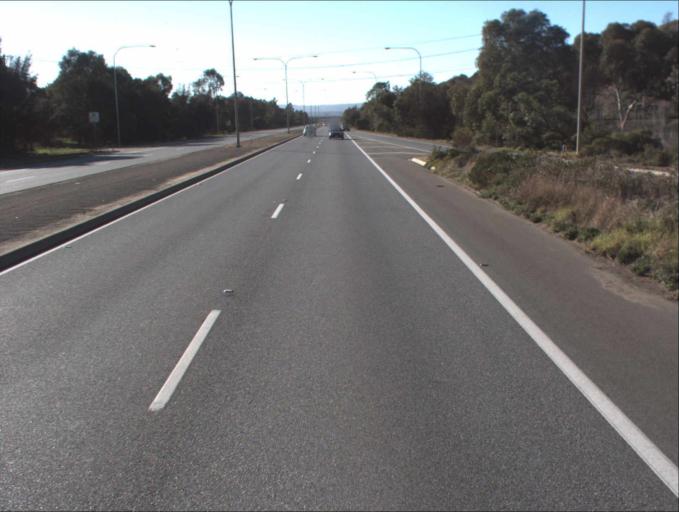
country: AU
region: South Australia
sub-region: Port Adelaide Enfield
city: Alberton
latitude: -34.8336
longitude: 138.5491
